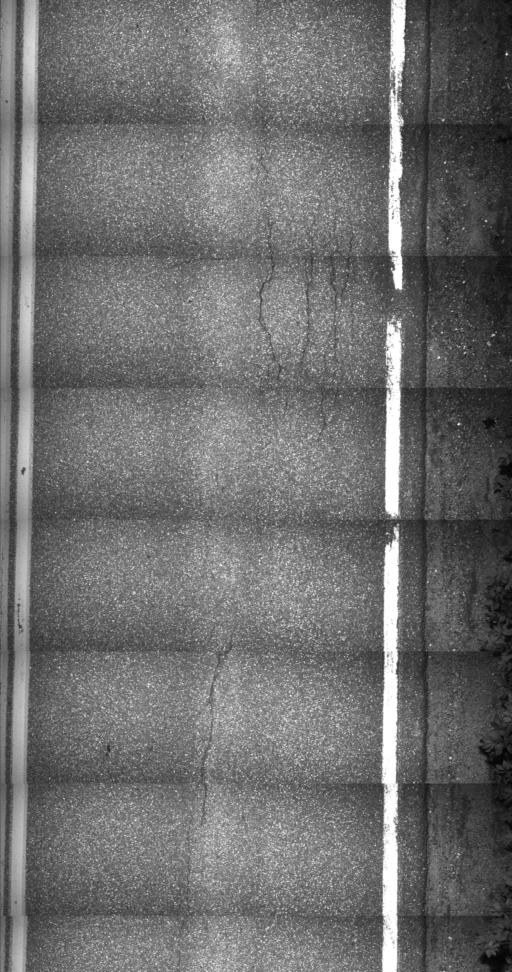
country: US
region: Vermont
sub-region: Washington County
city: Barre
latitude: 44.2539
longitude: -72.2681
